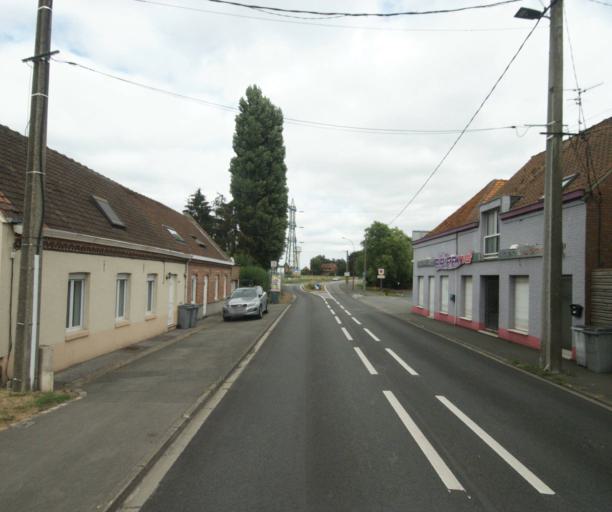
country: FR
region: Nord-Pas-de-Calais
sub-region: Departement du Nord
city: Toufflers
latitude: 50.6756
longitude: 3.2297
